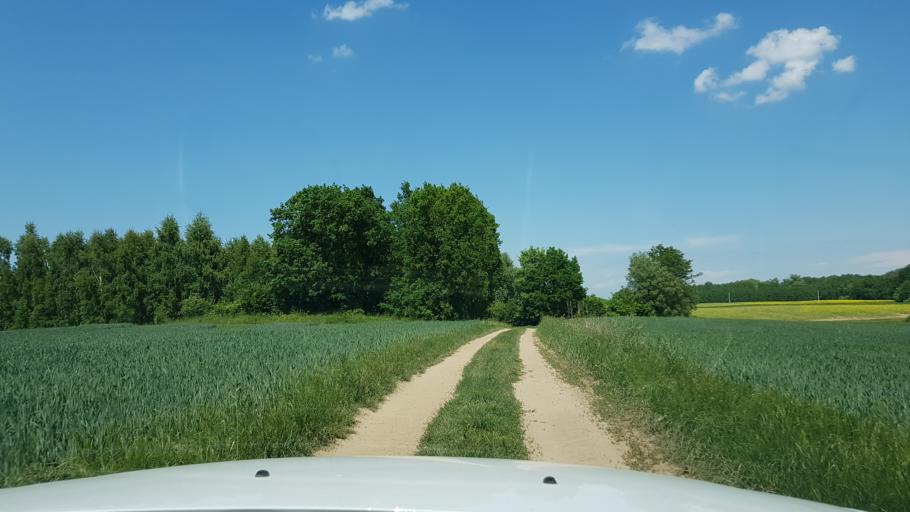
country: PL
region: West Pomeranian Voivodeship
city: Trzcinsko Zdroj
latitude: 52.9368
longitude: 14.5789
